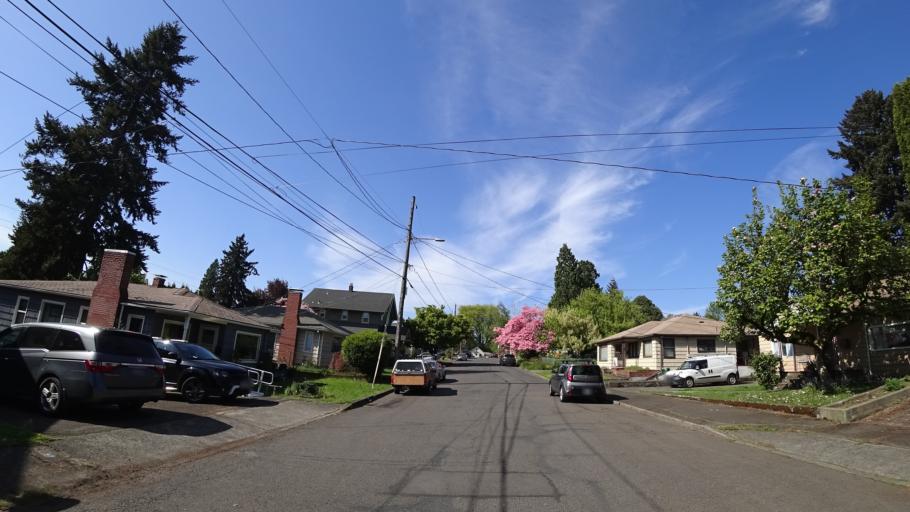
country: US
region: Oregon
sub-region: Clackamas County
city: Milwaukie
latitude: 45.4591
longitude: -122.6318
